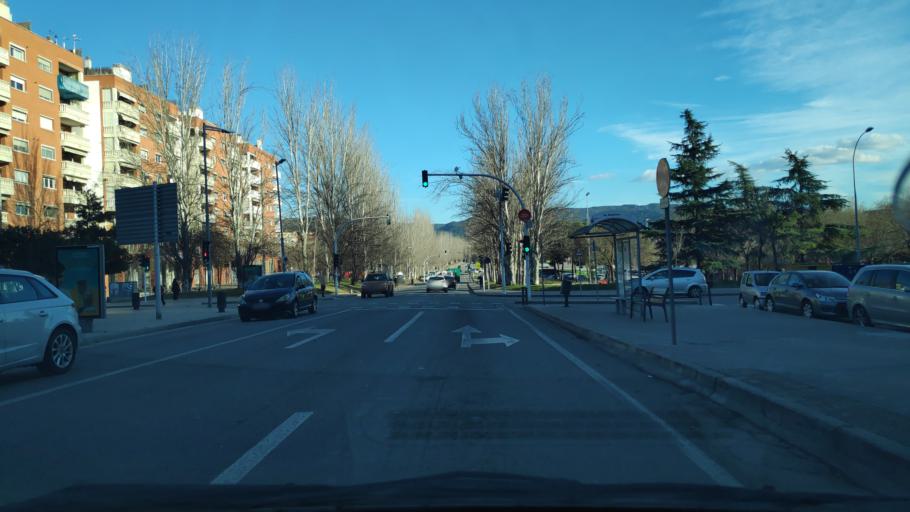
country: ES
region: Catalonia
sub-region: Provincia de Barcelona
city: Mollet del Valles
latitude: 41.5344
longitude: 2.2102
